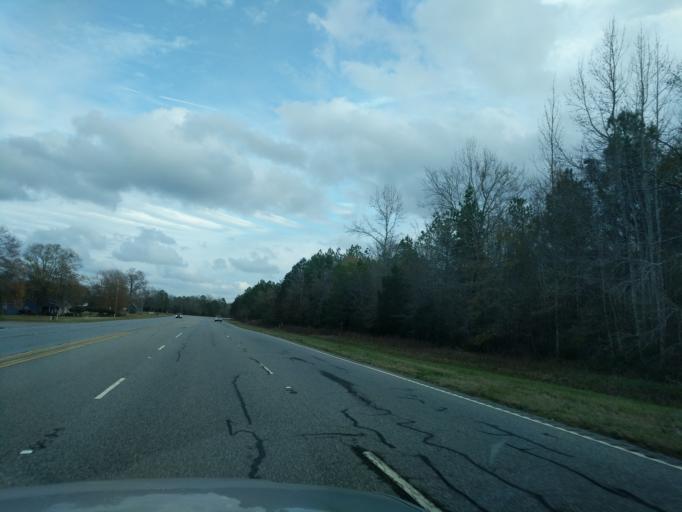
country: US
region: South Carolina
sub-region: Greenwood County
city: Ware Shoals
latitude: 34.4680
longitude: -82.2658
